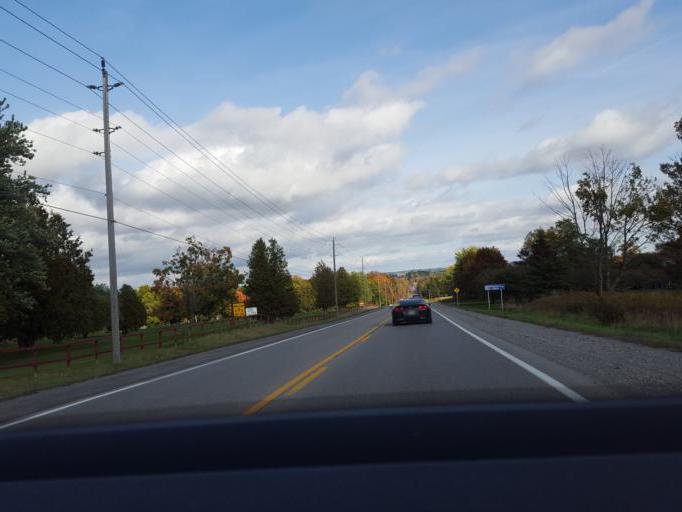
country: CA
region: Ontario
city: Oshawa
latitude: 43.9762
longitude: -78.6919
